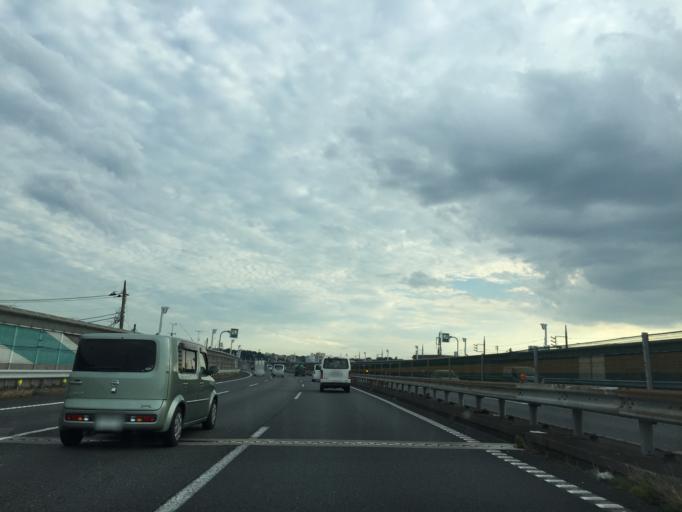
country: JP
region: Tokyo
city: Chofugaoka
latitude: 35.6237
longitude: 139.6002
